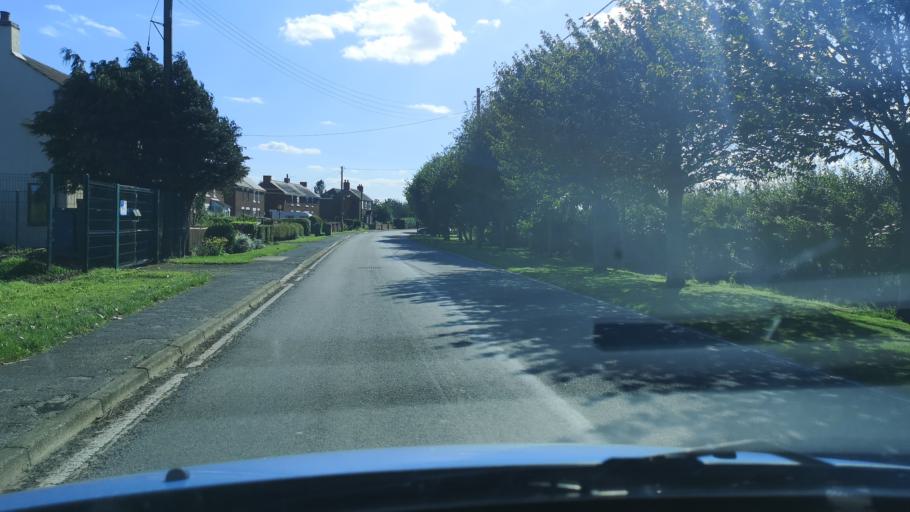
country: GB
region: England
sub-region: North Lincolnshire
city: Eastoft
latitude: 53.6349
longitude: -0.7511
